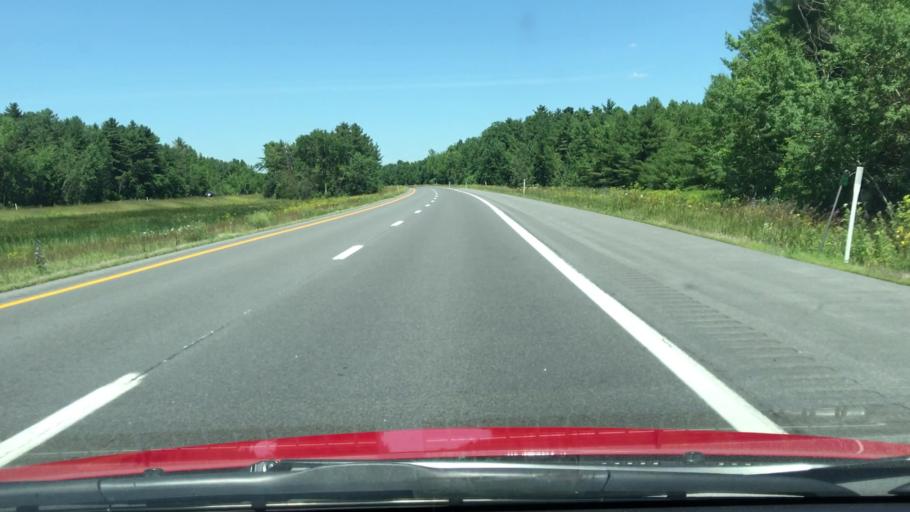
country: US
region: New York
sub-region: Clinton County
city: Cumberland Head
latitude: 44.8406
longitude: -73.4463
